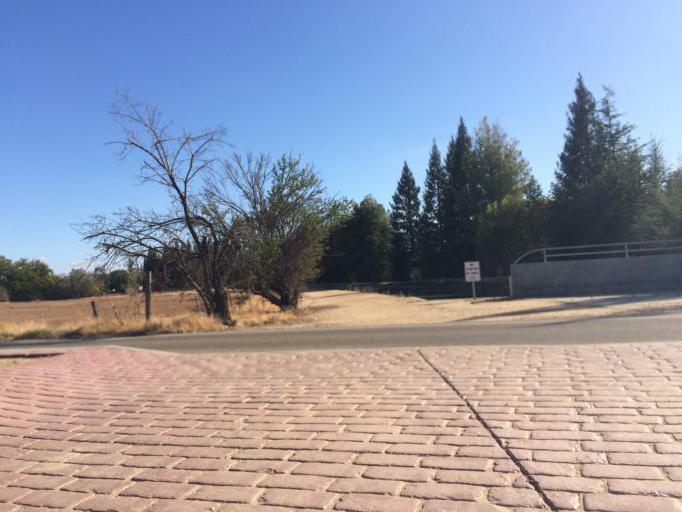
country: US
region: California
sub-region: Fresno County
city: Clovis
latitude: 36.8520
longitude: -119.6686
